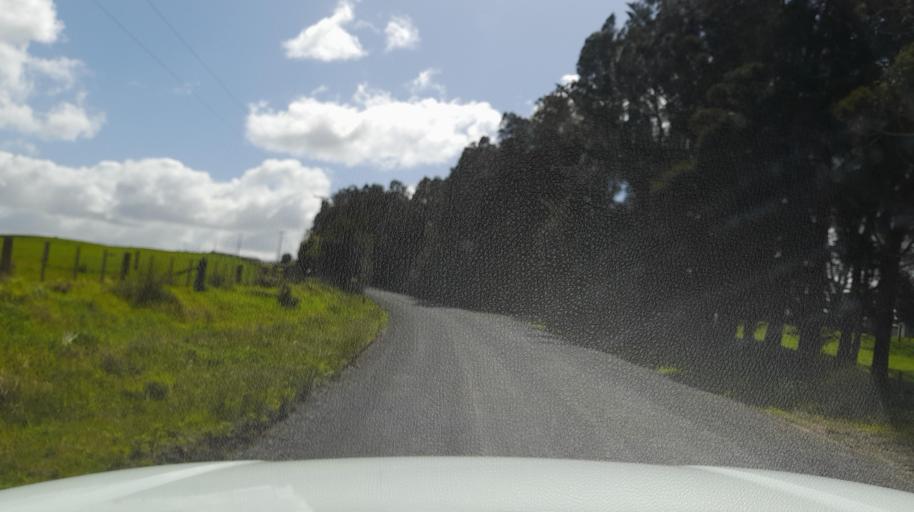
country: NZ
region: Northland
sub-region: Far North District
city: Kerikeri
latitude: -35.2259
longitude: 173.8756
